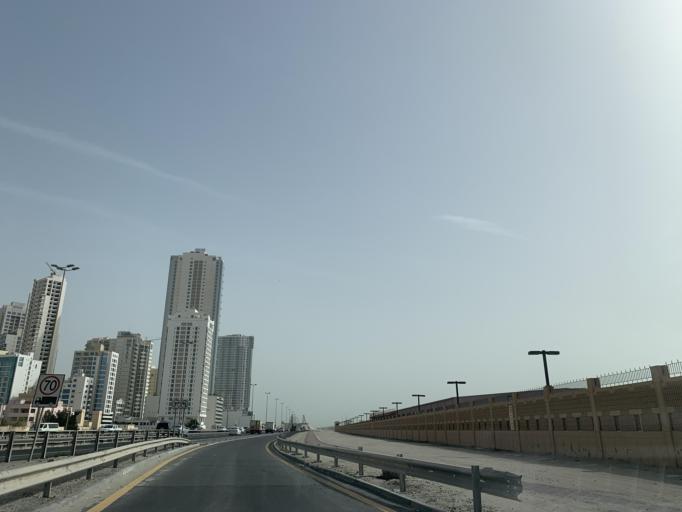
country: BH
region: Manama
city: Manama
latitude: 26.2090
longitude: 50.6165
